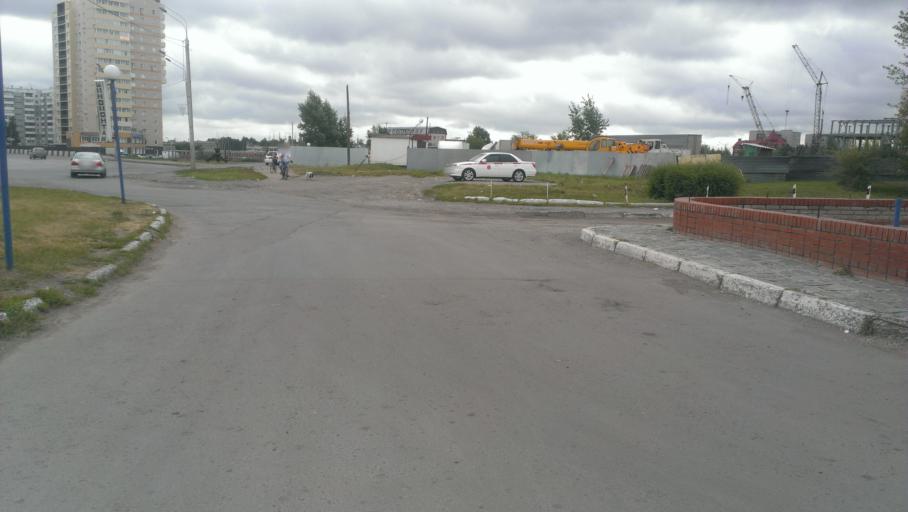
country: RU
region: Altai Krai
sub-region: Gorod Barnaulskiy
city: Barnaul
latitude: 53.3415
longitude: 83.6931
